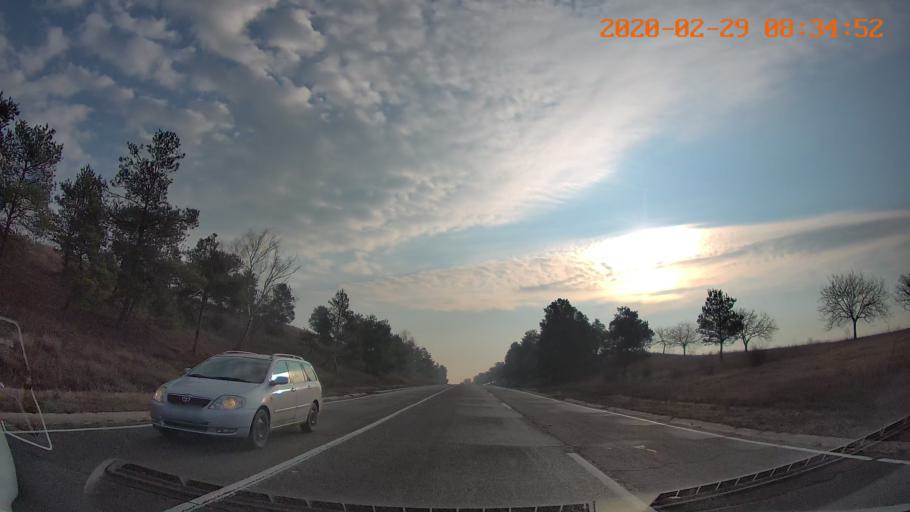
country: MD
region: Anenii Noi
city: Anenii Noi
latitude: 46.9237
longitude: 29.3171
